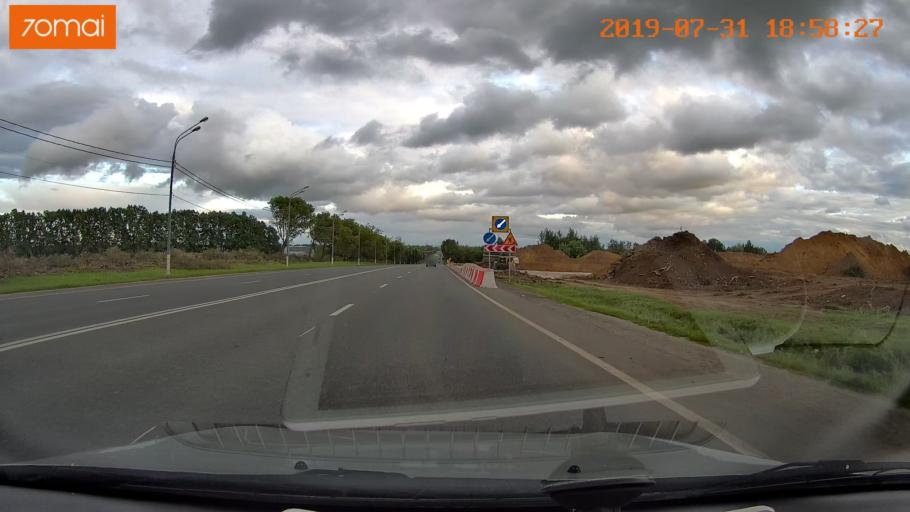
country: RU
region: Moskovskaya
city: Raduzhnyy
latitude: 55.1467
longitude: 38.7047
